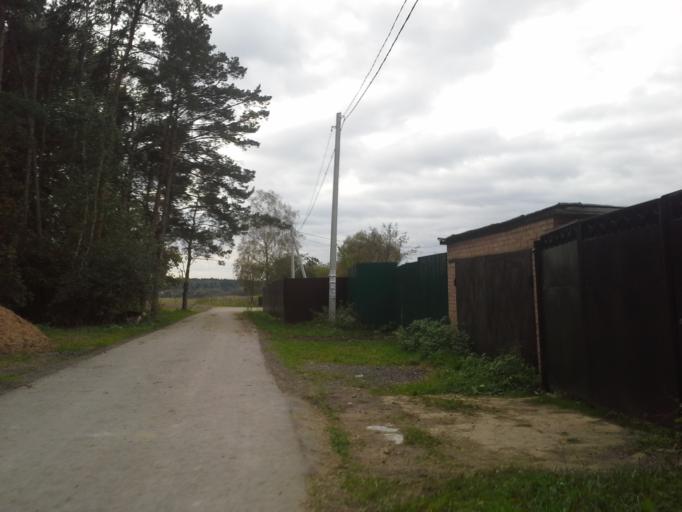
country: RU
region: Moskovskaya
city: Kokoshkino
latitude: 55.6090
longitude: 37.1593
